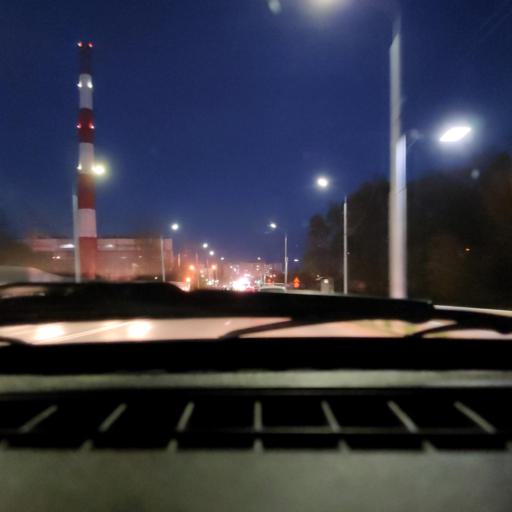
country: RU
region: Bashkortostan
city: Ufa
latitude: 54.7887
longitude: 56.1129
